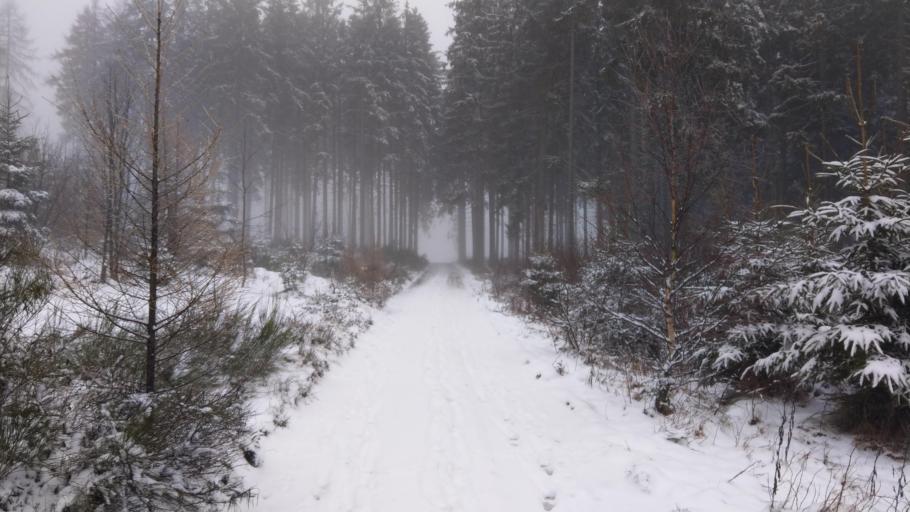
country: DE
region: North Rhine-Westphalia
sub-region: Regierungsbezirk Arnsberg
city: Erndtebruck
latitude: 50.9851
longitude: 8.2162
